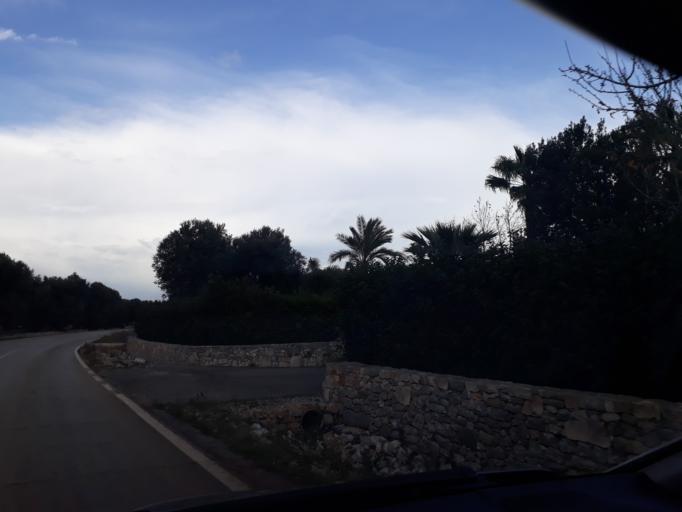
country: IT
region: Apulia
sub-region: Provincia di Brindisi
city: Pezze di Greco
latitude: 40.8130
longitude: 17.3824
